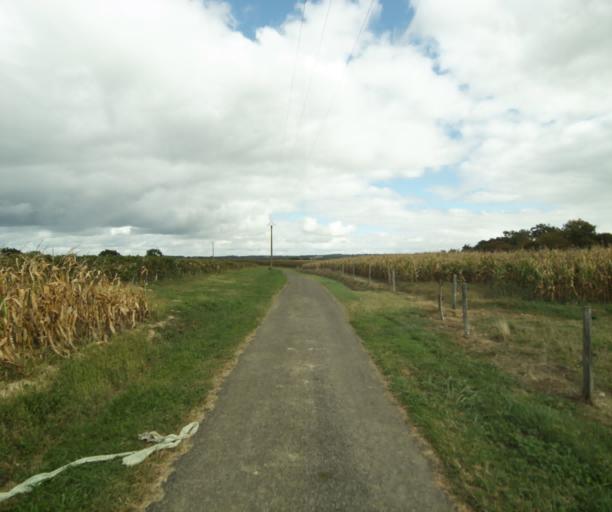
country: FR
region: Midi-Pyrenees
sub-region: Departement du Gers
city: Cazaubon
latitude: 43.8656
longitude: -0.0344
